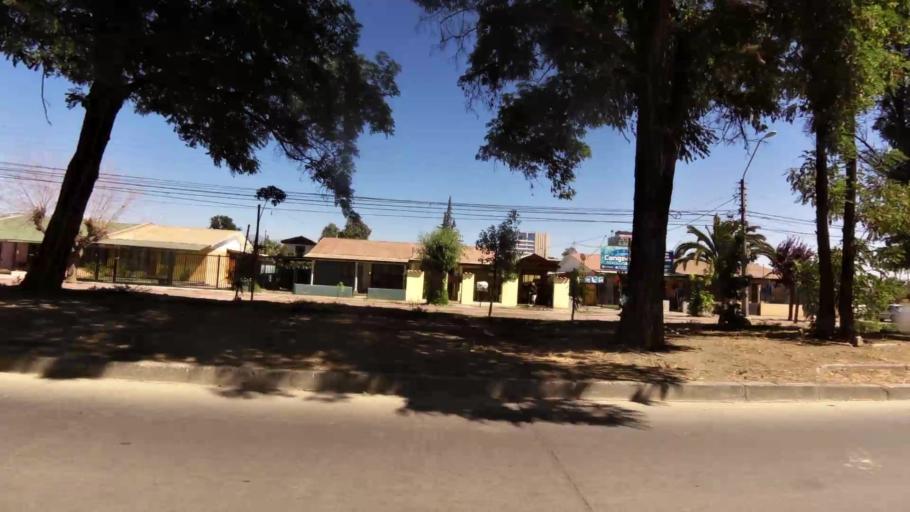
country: CL
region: O'Higgins
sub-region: Provincia de Cachapoal
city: Rancagua
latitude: -34.1757
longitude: -70.7134
